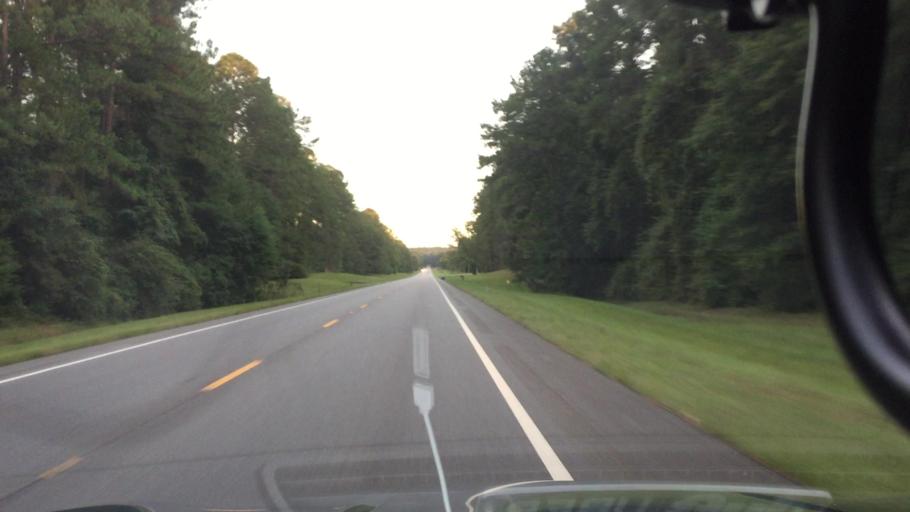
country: US
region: Alabama
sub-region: Coffee County
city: New Brockton
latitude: 31.4842
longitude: -85.9112
